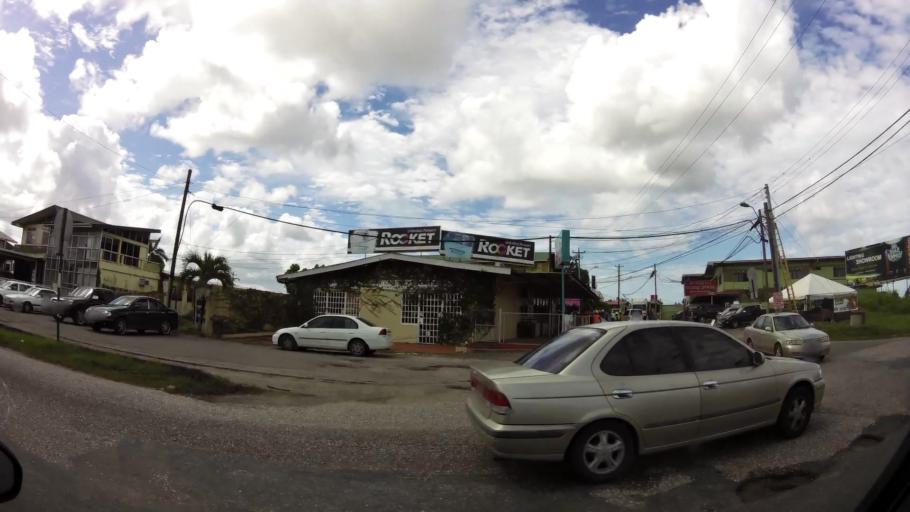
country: TT
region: City of San Fernando
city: Marabella
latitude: 10.2988
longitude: -61.4482
